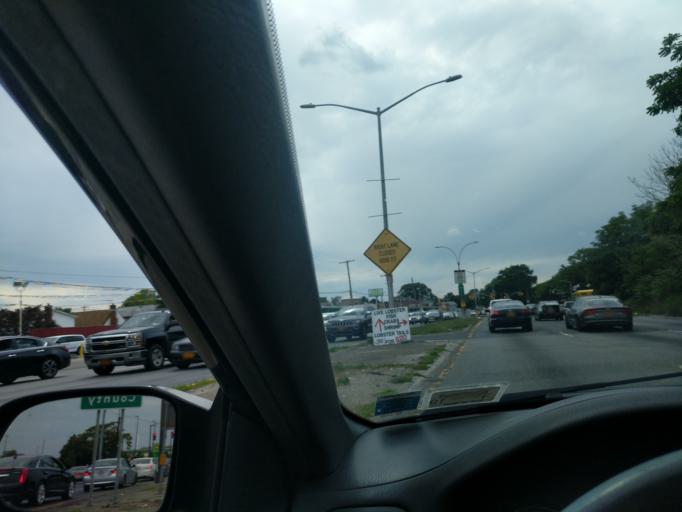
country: US
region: New York
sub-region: Nassau County
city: South Valley Stream
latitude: 40.6655
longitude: -73.7281
